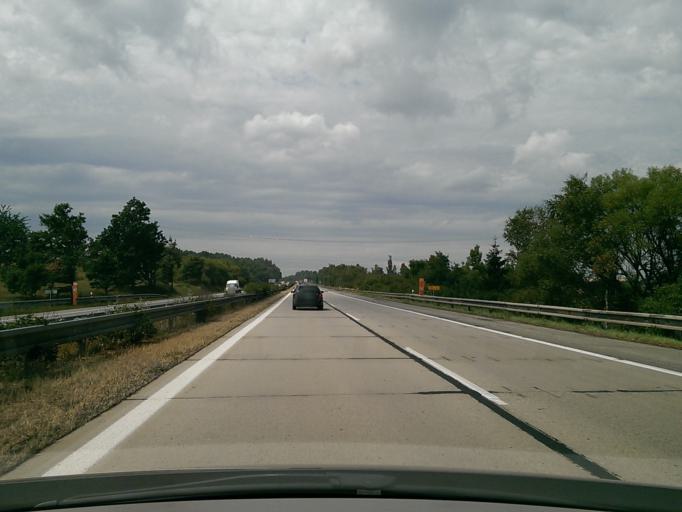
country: CZ
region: Vysocina
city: Merin
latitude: 49.4021
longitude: 15.8524
